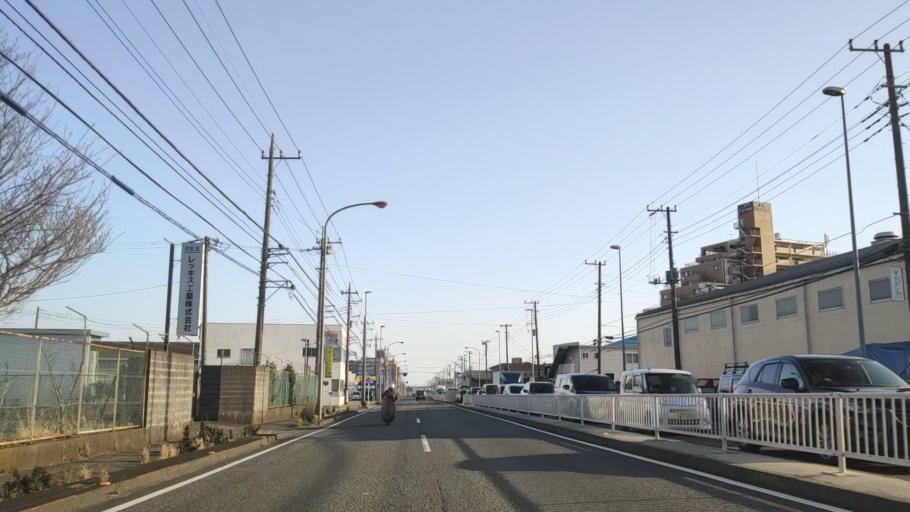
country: JP
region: Kanagawa
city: Zama
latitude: 35.4842
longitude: 139.3654
